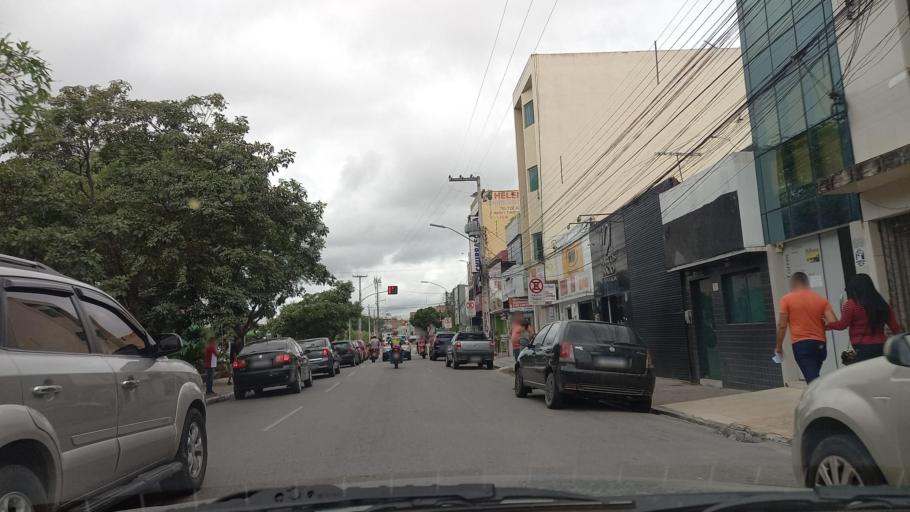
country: BR
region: Pernambuco
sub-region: Caruaru
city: Caruaru
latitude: -8.2803
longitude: -35.9745
